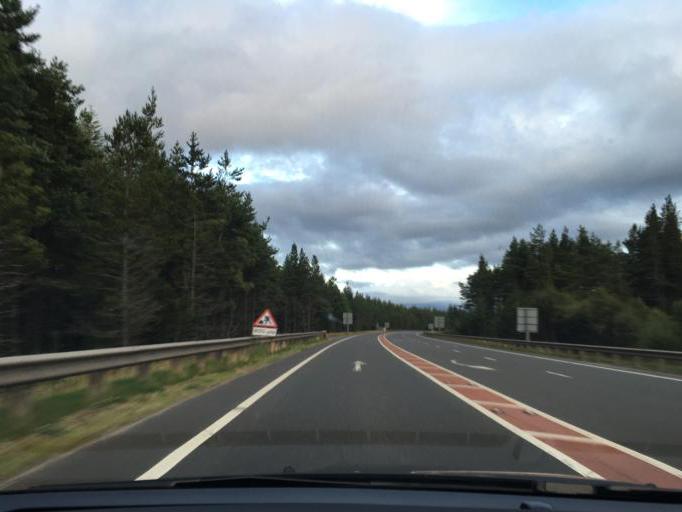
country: GB
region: Scotland
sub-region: Highland
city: Inverness
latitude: 57.3789
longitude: -4.0450
